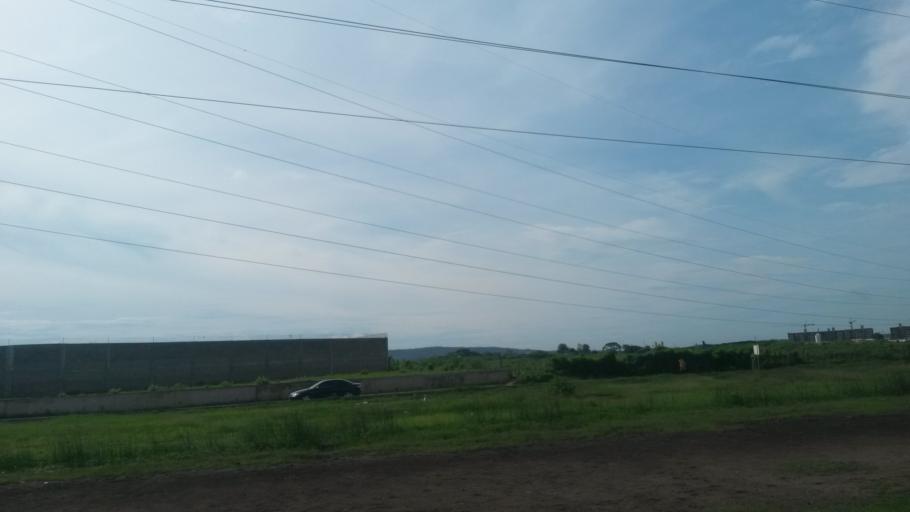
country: CO
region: Bolivar
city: Cartagena
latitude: 10.4061
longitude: -75.4528
